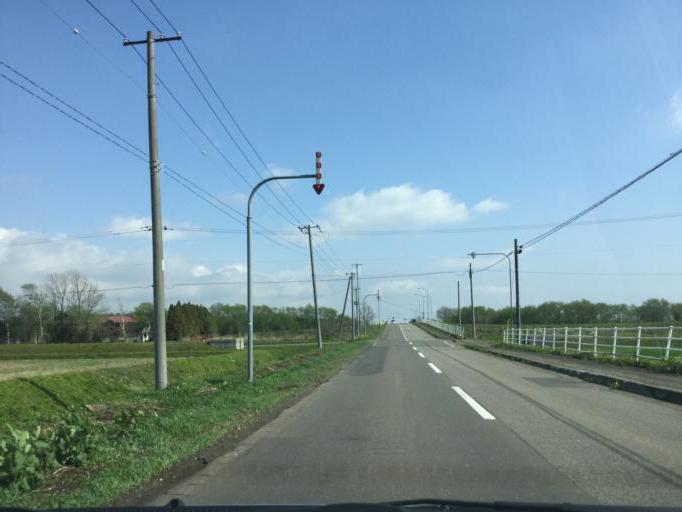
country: JP
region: Hokkaido
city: Iwamizawa
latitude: 43.1474
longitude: 141.7192
